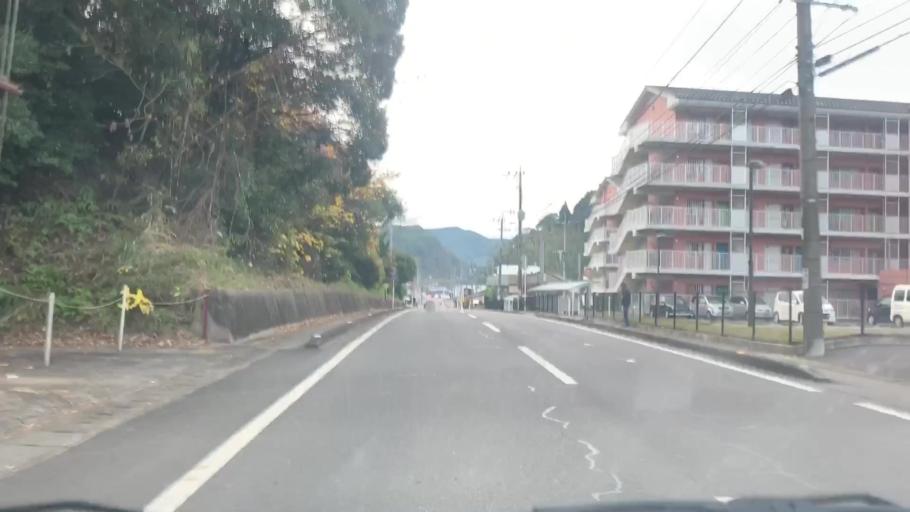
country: JP
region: Saga Prefecture
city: Takeocho-takeo
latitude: 33.1892
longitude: 130.0362
